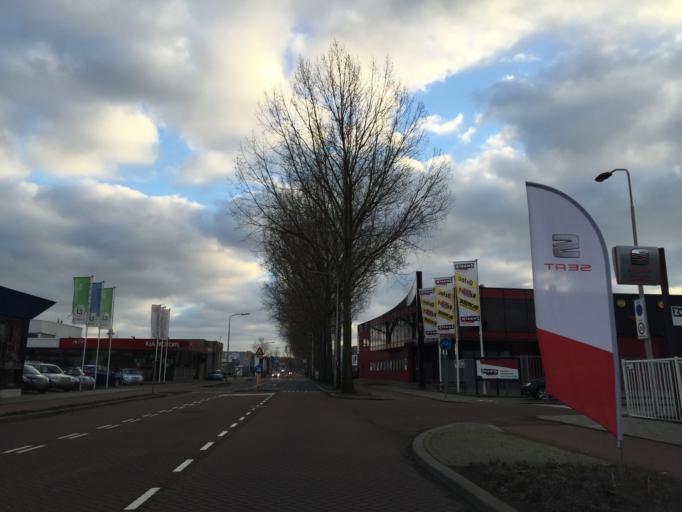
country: NL
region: South Holland
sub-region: Gemeente Delft
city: Delft
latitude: 51.9877
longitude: 4.3695
